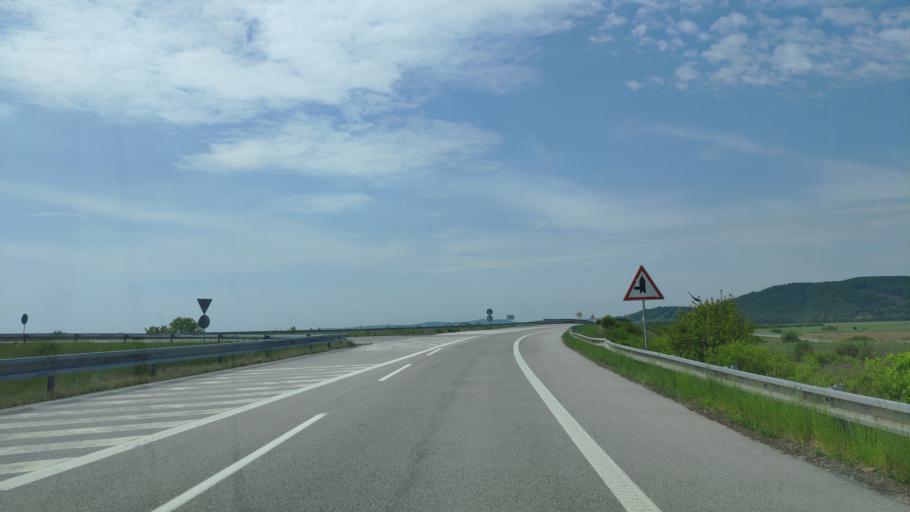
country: HU
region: Borsod-Abauj-Zemplen
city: Putnok
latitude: 48.4505
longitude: 20.3446
